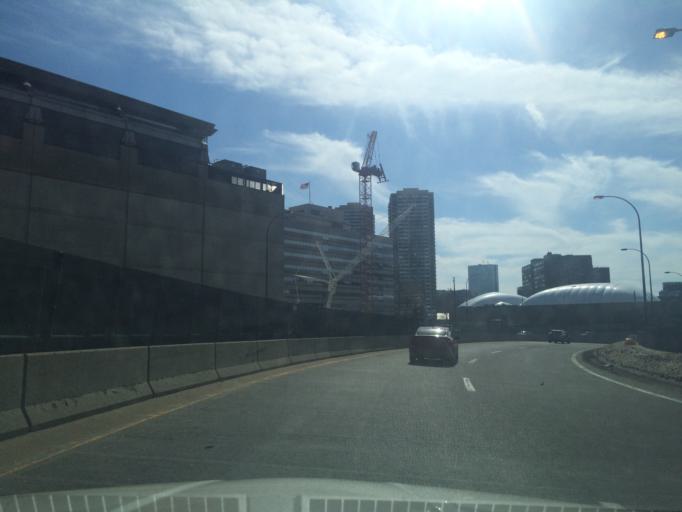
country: US
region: Massachusetts
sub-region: Suffolk County
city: Boston
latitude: 42.3673
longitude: -71.0631
